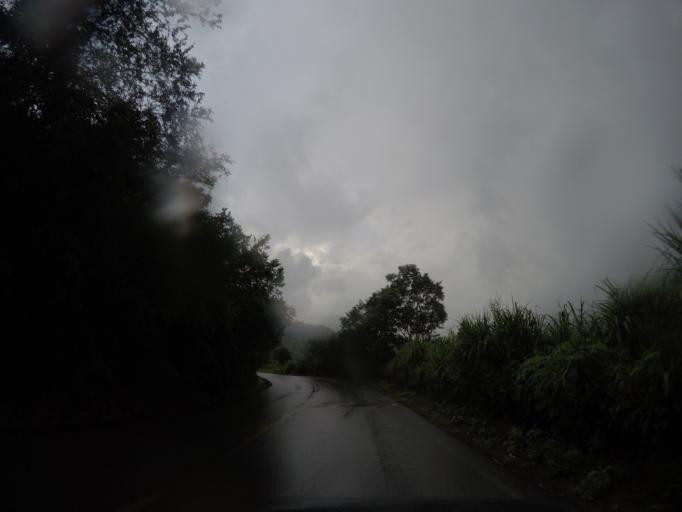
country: MX
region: Oaxaca
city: San Gabriel Mixtepec
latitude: 16.0740
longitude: -97.0828
